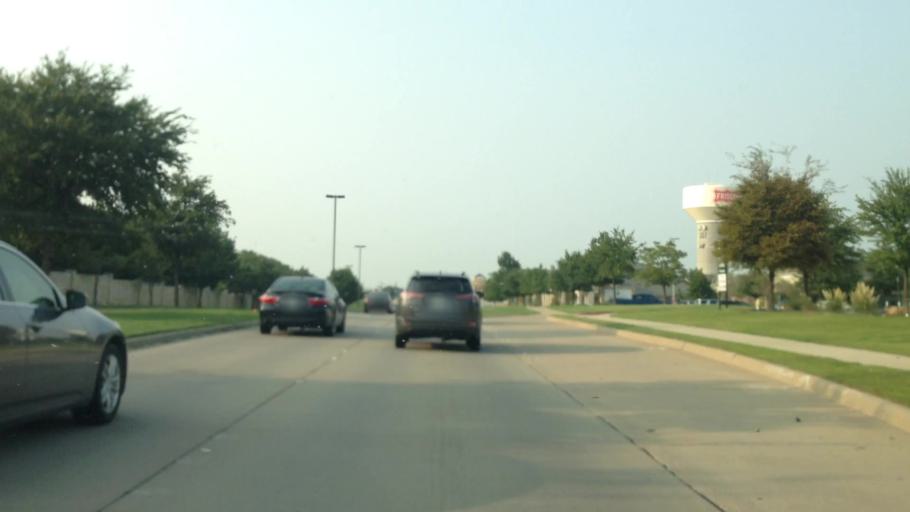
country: US
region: Texas
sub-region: Denton County
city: The Colony
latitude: 33.1020
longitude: -96.8416
